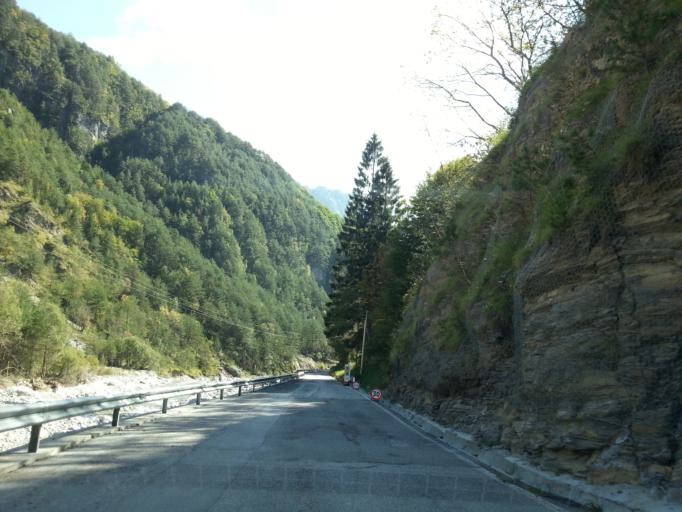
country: IT
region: Friuli Venezia Giulia
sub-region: Provincia di Udine
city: Moggio Udinese
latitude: 46.4757
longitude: 13.1894
